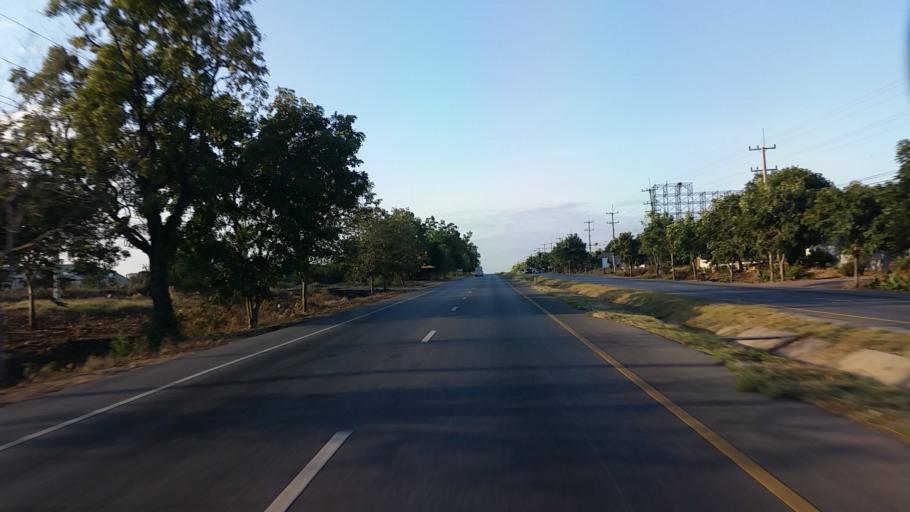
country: TH
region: Lop Buri
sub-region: Amphoe Tha Luang
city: Tha Luang
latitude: 15.1380
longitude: 101.0444
